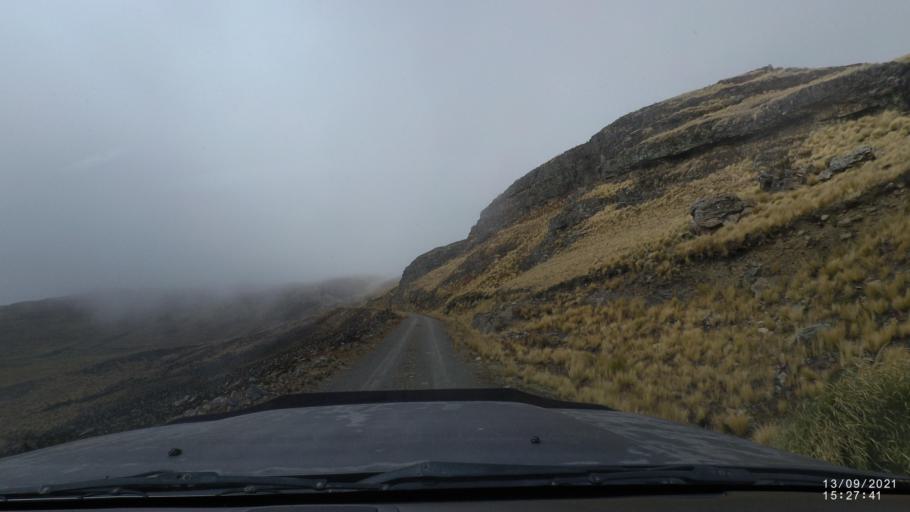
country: BO
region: Cochabamba
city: Colomi
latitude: -17.3500
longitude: -65.7606
